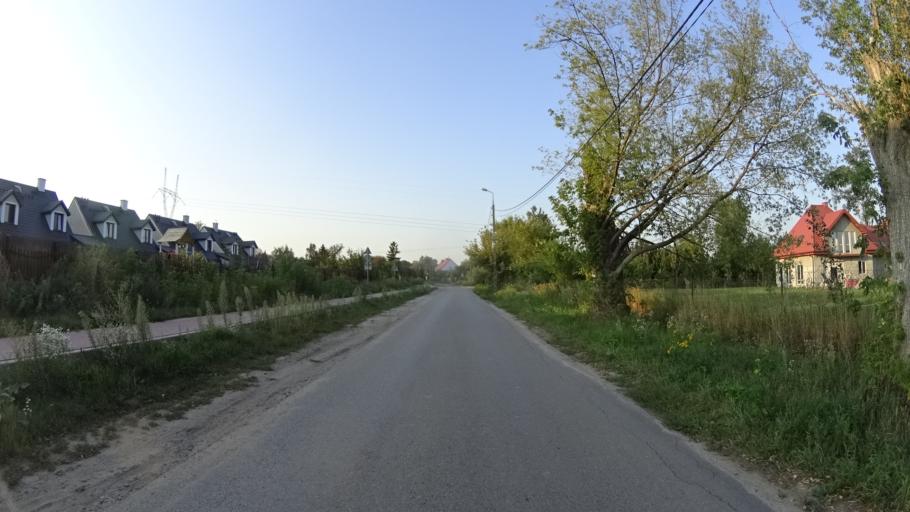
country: PL
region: Masovian Voivodeship
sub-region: Powiat warszawski zachodni
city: Ozarow Mazowiecki
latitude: 52.2363
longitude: 20.7811
